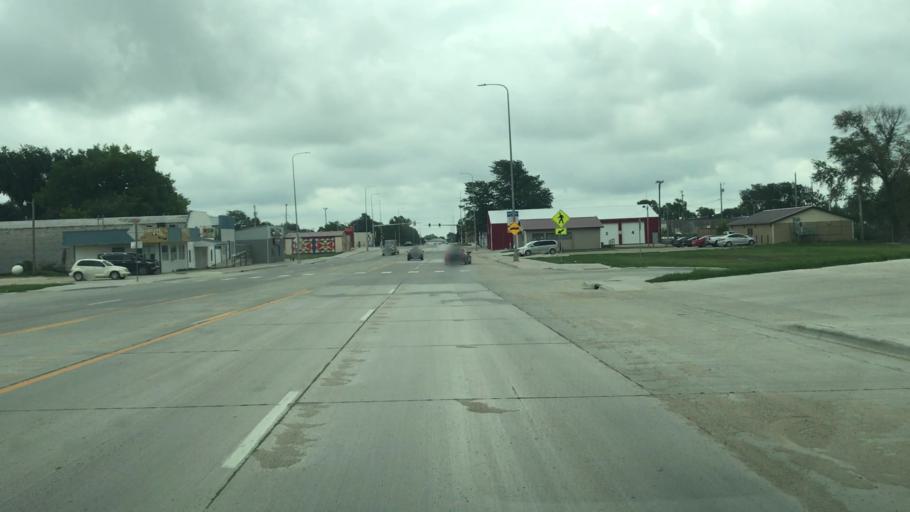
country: US
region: South Dakota
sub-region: Todd County
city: Mission
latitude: 43.3057
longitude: -100.6619
